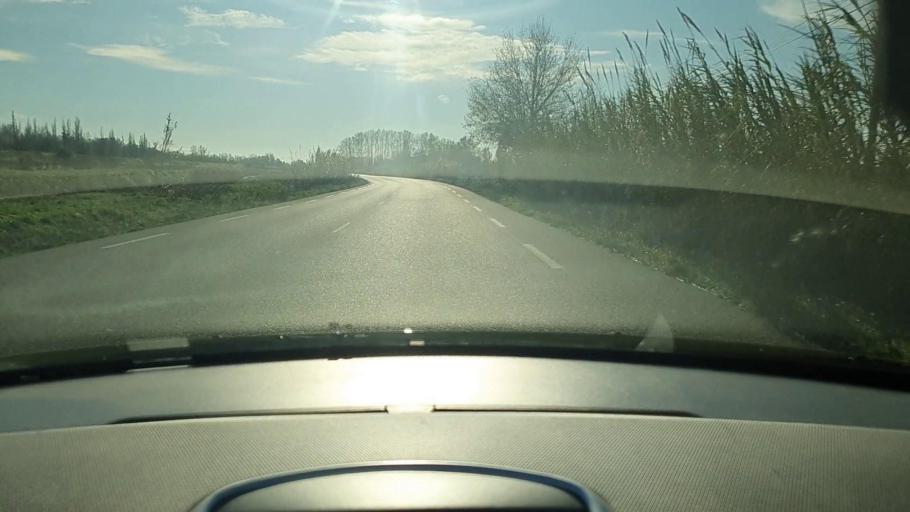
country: FR
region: Languedoc-Roussillon
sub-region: Departement du Gard
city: Fourques
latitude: 43.7337
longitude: 4.6102
